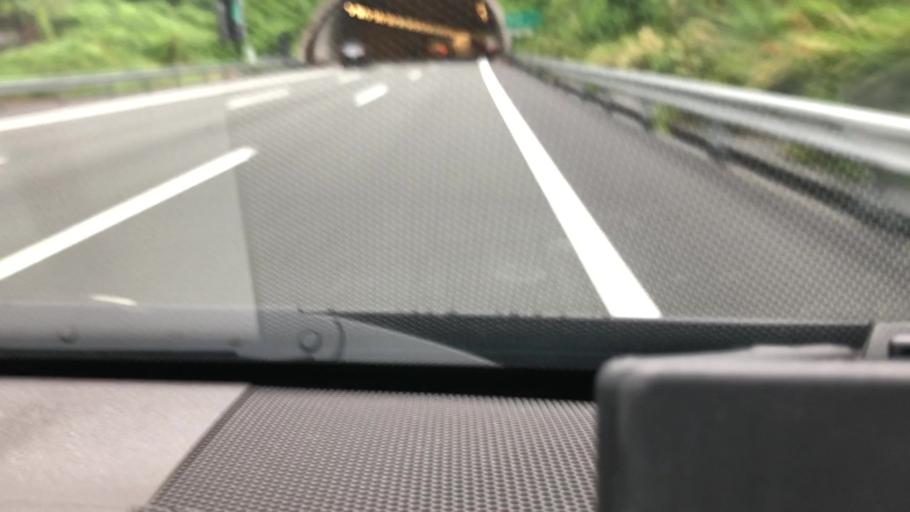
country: JP
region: Shizuoka
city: Shizuoka-shi
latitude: 35.0059
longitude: 138.3106
